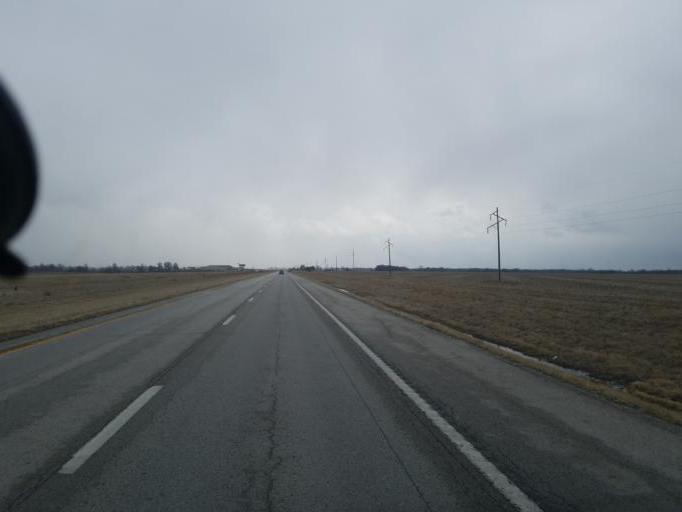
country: US
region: Missouri
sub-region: Randolph County
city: Moberly
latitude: 39.5528
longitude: -92.4557
